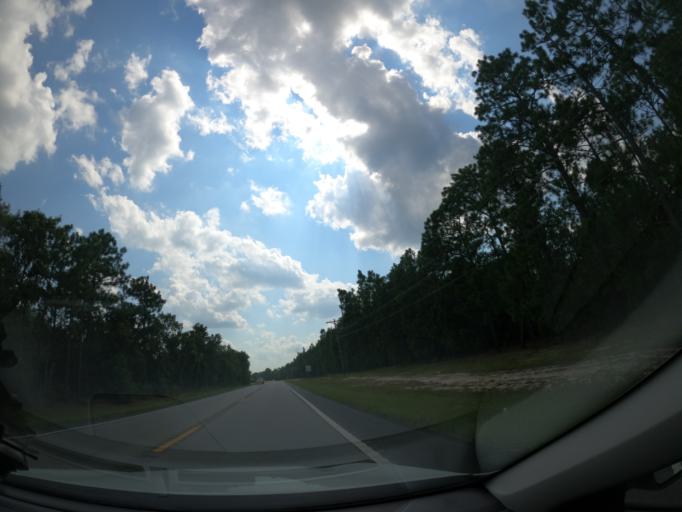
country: US
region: South Carolina
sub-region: Lexington County
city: South Congaree
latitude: 33.8658
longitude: -81.1971
